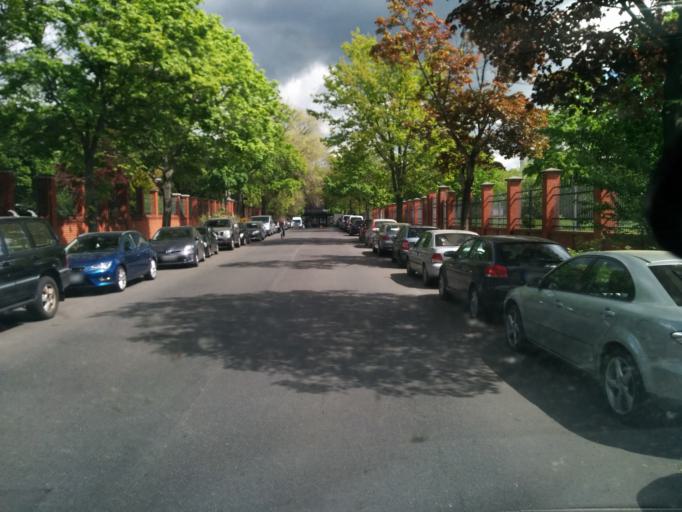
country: DE
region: Berlin
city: Gesundbrunnen
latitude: 52.5390
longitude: 13.3774
